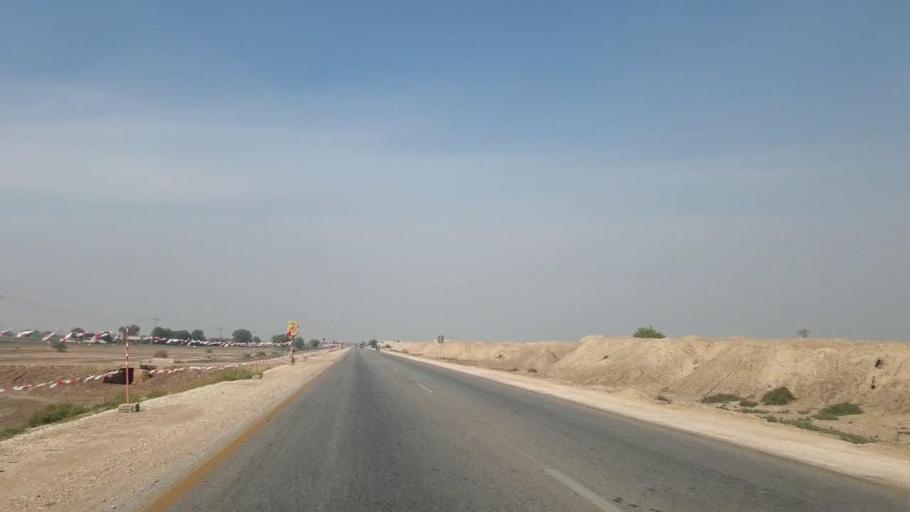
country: PK
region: Sindh
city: Sann
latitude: 25.9694
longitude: 68.1888
